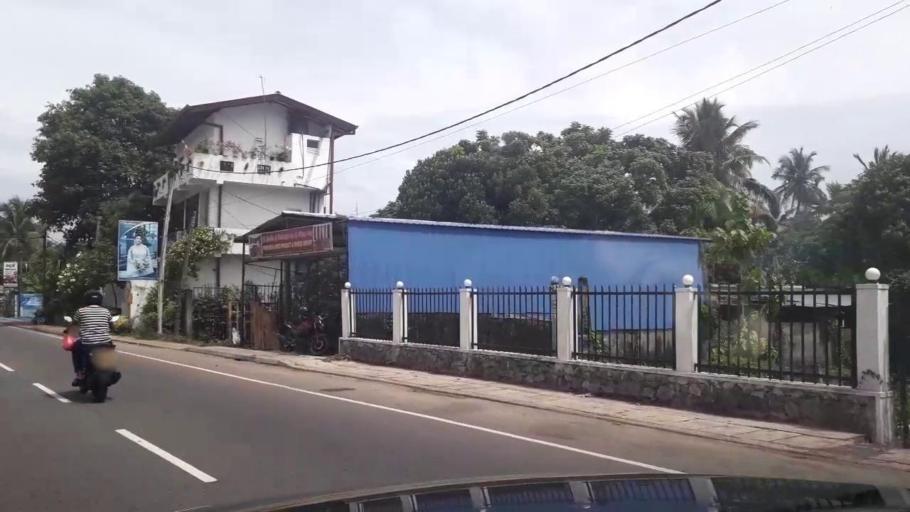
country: LK
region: Western
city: Moratuwa
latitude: 6.7581
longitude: 79.8984
